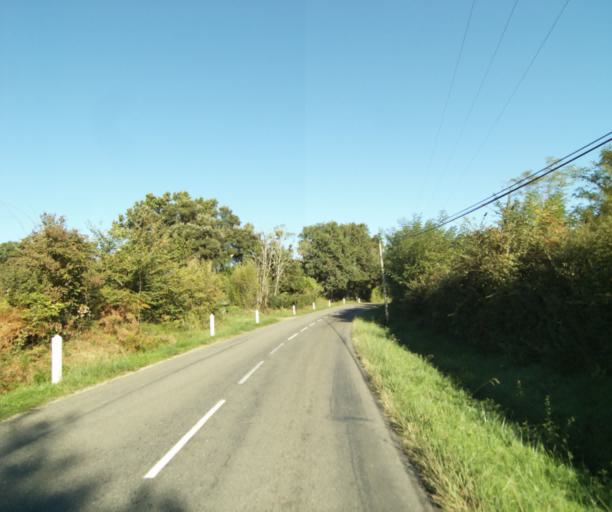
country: FR
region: Aquitaine
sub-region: Departement des Landes
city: Gabarret
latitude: 43.9371
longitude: 0.0143
